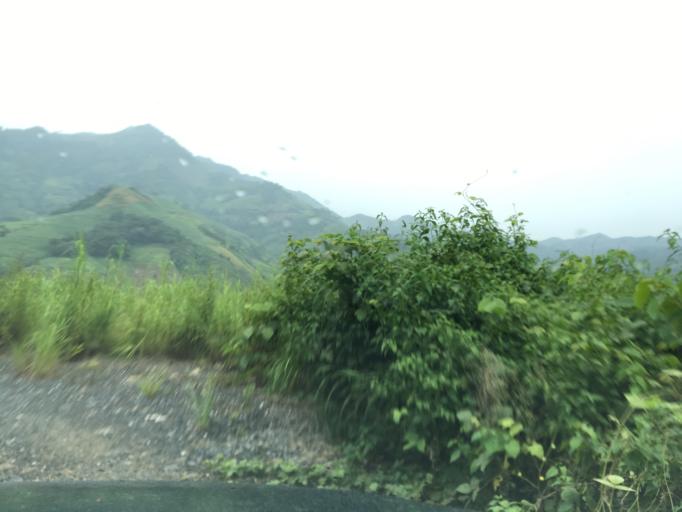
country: CN
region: Guangxi Zhuangzu Zizhiqu
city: Tongle
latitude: 25.0014
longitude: 105.9974
